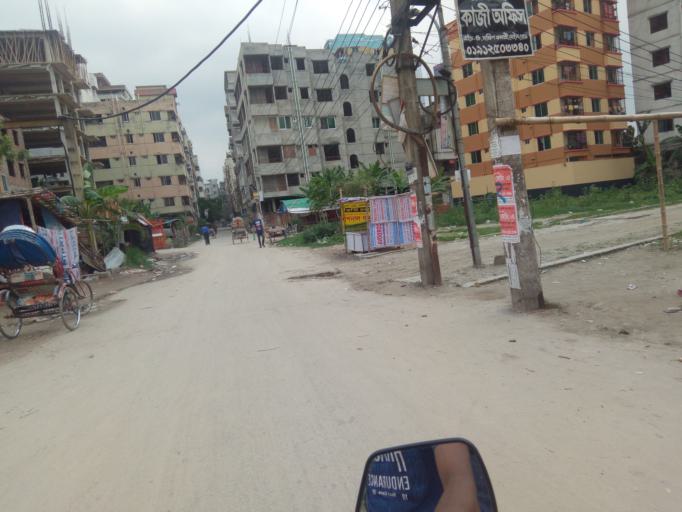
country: BD
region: Dhaka
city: Paltan
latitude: 23.7529
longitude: 90.4385
